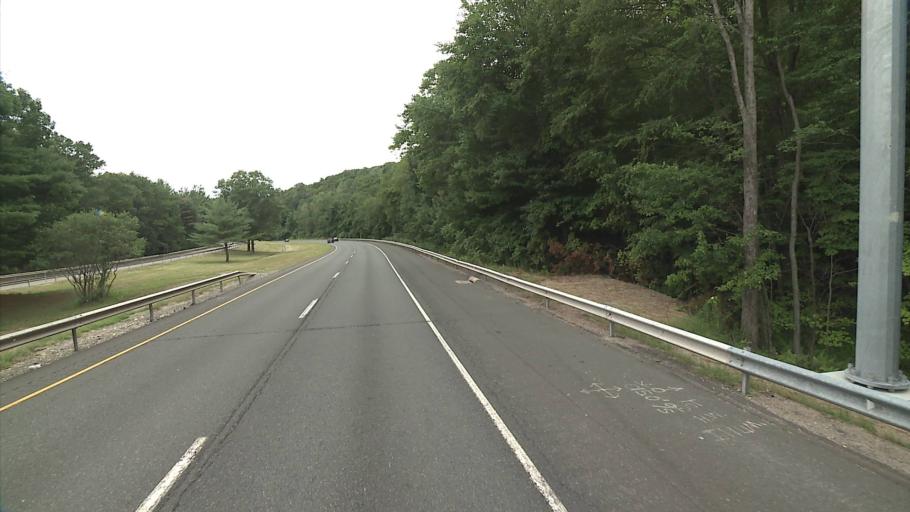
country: US
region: Connecticut
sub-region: Litchfield County
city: Thomaston
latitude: 41.6913
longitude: -73.0700
